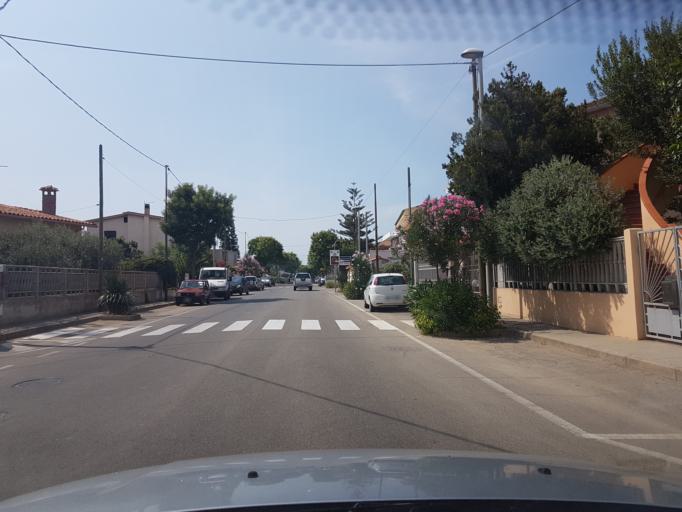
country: IT
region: Sardinia
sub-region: Provincia di Oristano
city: Cabras
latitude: 39.9229
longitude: 8.5418
